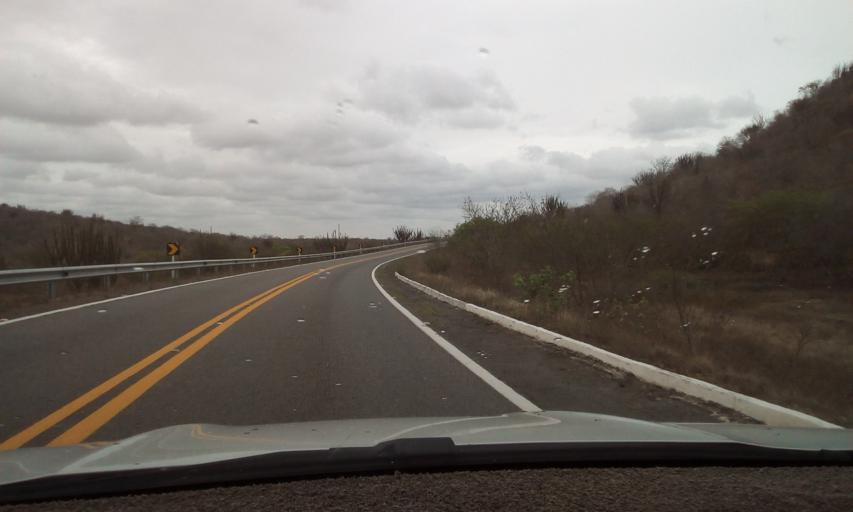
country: BR
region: Paraiba
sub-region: Areia
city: Remigio
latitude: -6.8871
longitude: -35.9199
